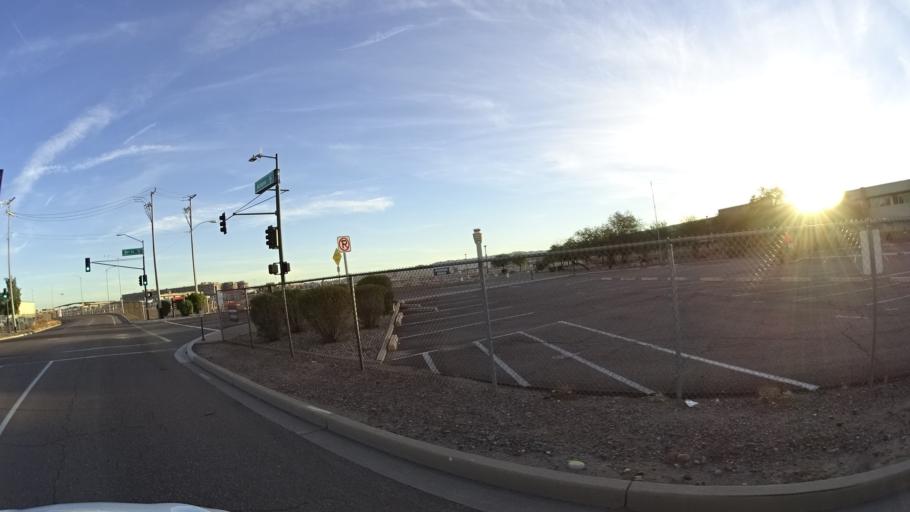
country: US
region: Arizona
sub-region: Maricopa County
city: Tempe Junction
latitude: 33.4435
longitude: -112.0041
